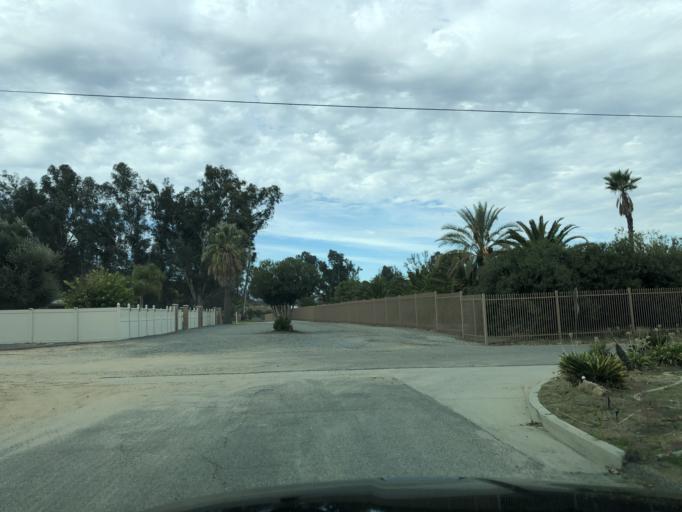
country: US
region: California
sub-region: Riverside County
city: Wildomar
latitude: 33.6004
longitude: -117.2866
